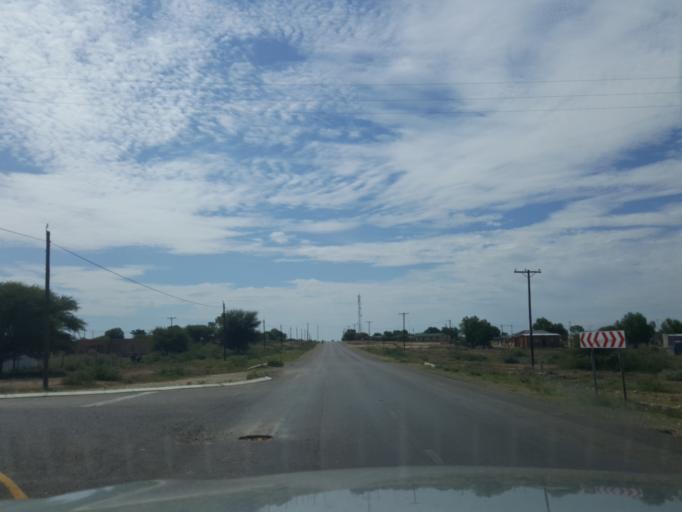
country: BW
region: Kweneng
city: Letlhakeng
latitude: -24.1082
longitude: 25.0336
